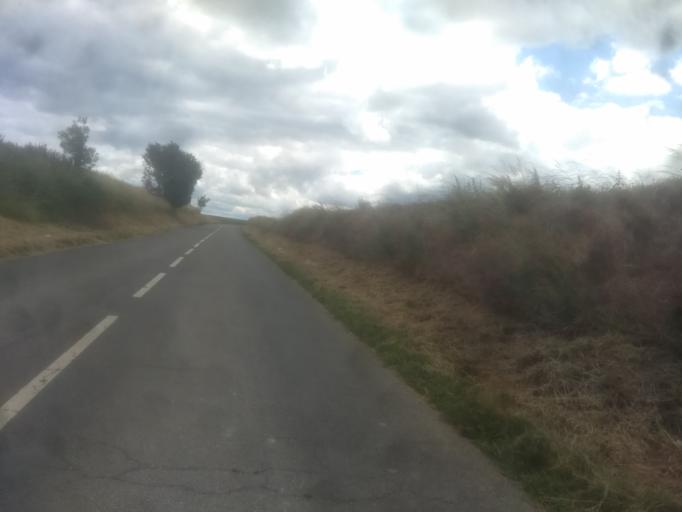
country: FR
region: Nord-Pas-de-Calais
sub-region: Departement du Pas-de-Calais
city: Agny
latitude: 50.2423
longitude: 2.7278
